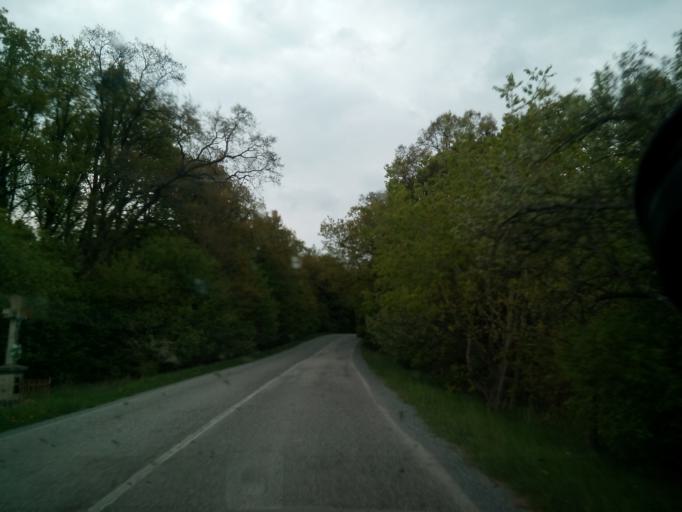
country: SK
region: Kosicky
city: Secovce
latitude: 48.7951
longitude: 21.4834
